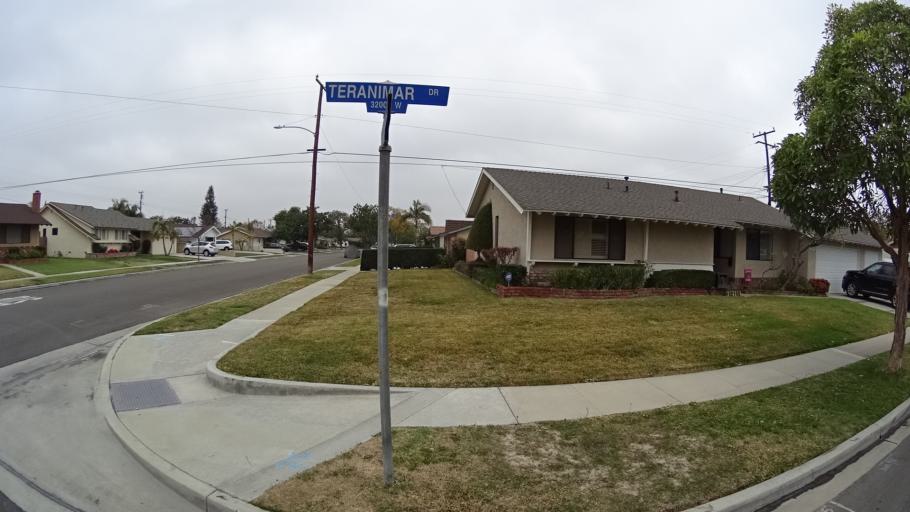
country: US
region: California
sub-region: Orange County
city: Stanton
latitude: 33.8196
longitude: -118.0047
